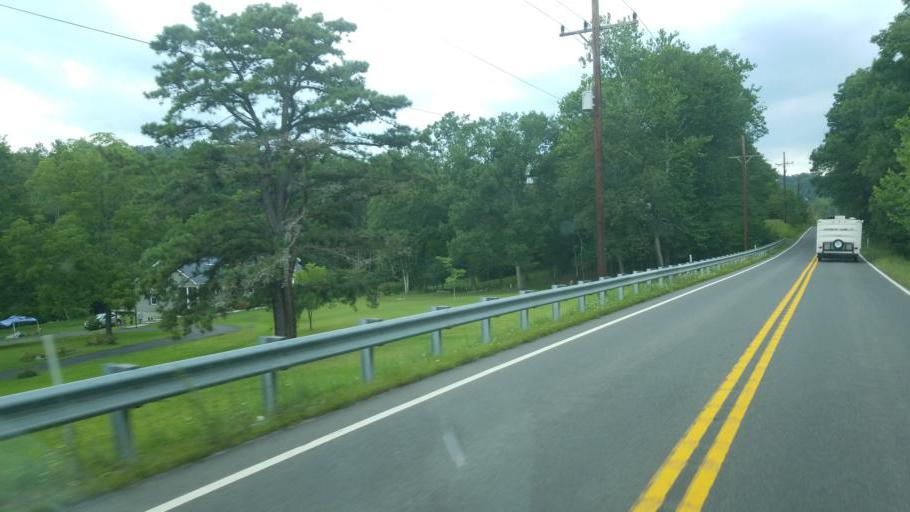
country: US
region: West Virginia
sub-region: Morgan County
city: Berkeley Springs
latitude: 39.5400
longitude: -78.4862
